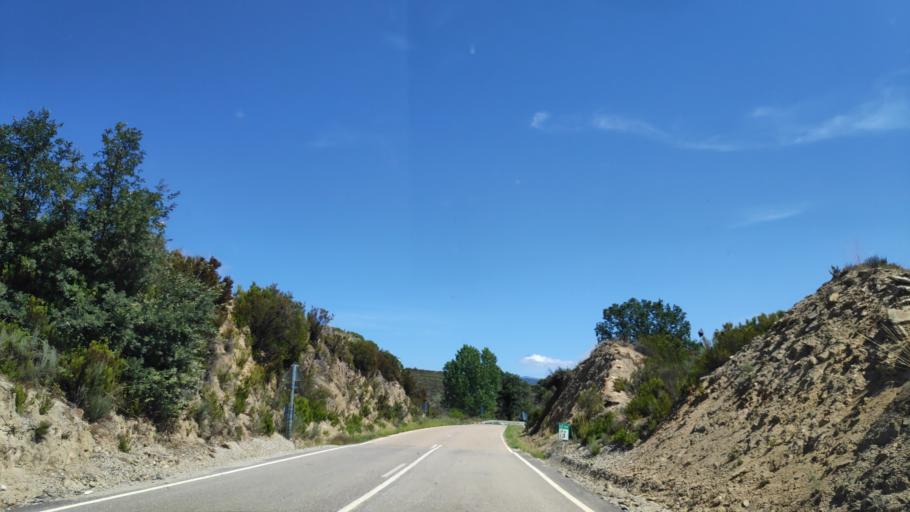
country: ES
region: Castille and Leon
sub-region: Provincia de Zamora
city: Puebla de Sanabria
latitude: 42.0473
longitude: -6.6466
